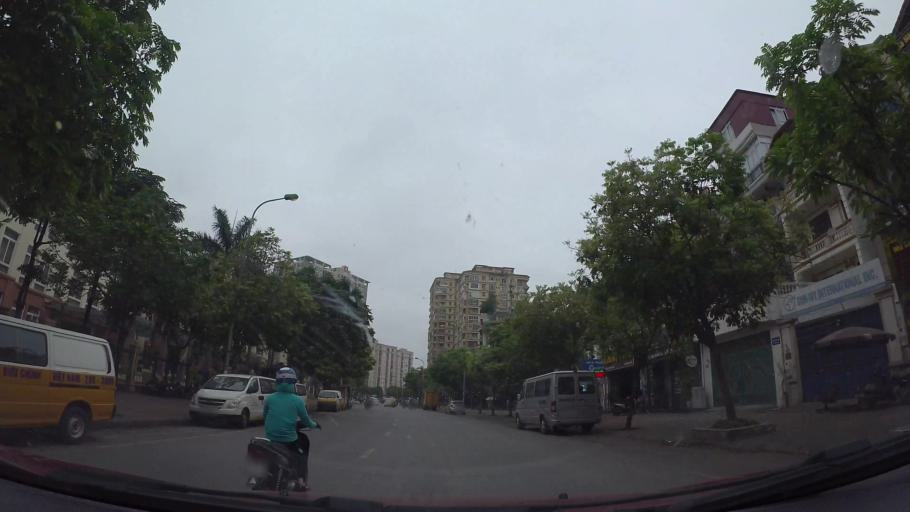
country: VN
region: Ha Noi
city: Cau Giay
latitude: 21.0162
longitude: 105.7980
